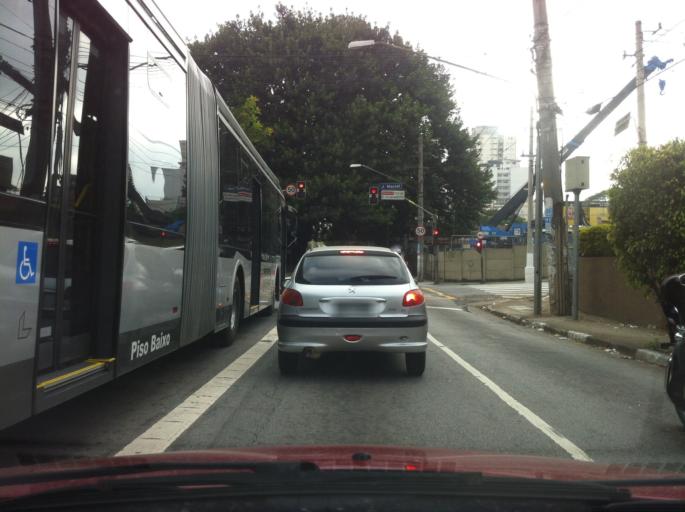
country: BR
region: Sao Paulo
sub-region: Sao Paulo
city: Sao Paulo
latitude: -23.6142
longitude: -46.6788
